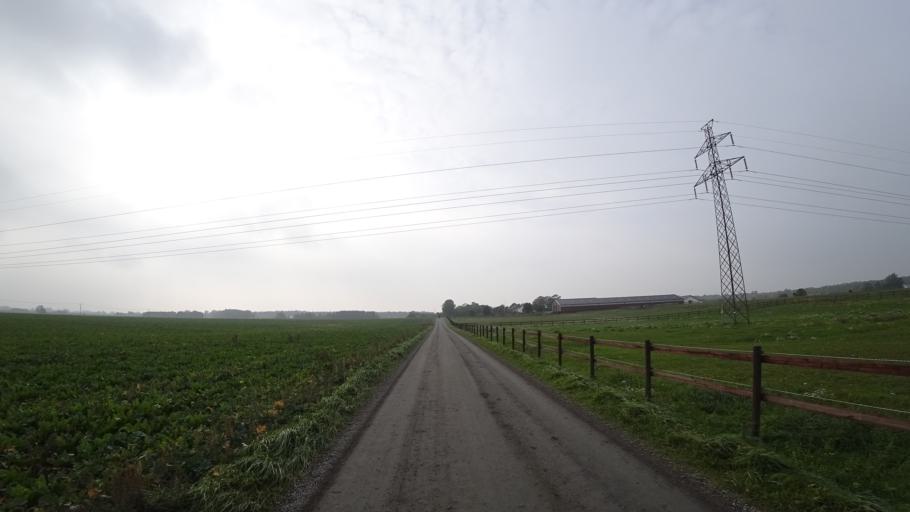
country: SE
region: Skane
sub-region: Kavlinge Kommun
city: Loddekopinge
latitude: 55.8081
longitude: 13.0036
